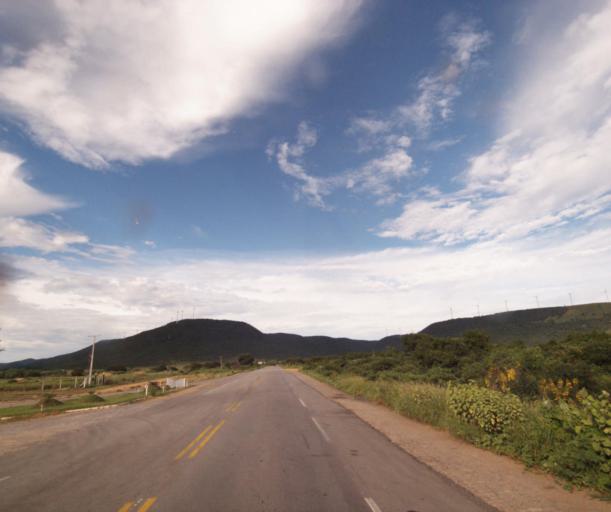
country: BR
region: Bahia
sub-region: Guanambi
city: Guanambi
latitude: -14.1669
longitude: -42.7219
